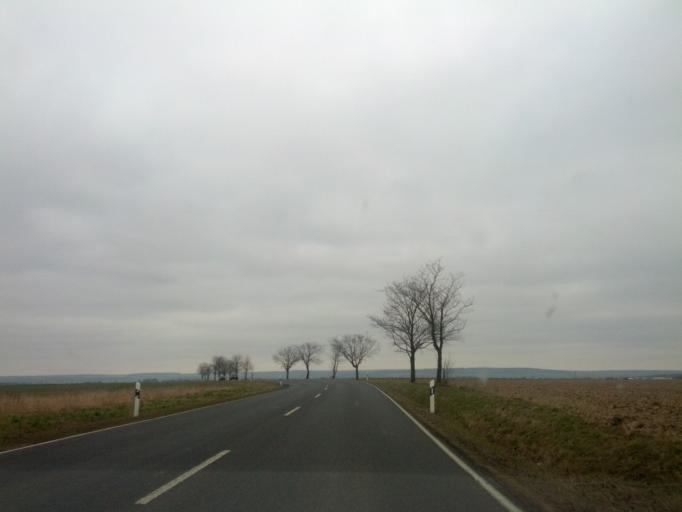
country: DE
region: Thuringia
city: Niederdorla
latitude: 51.1776
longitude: 10.4469
